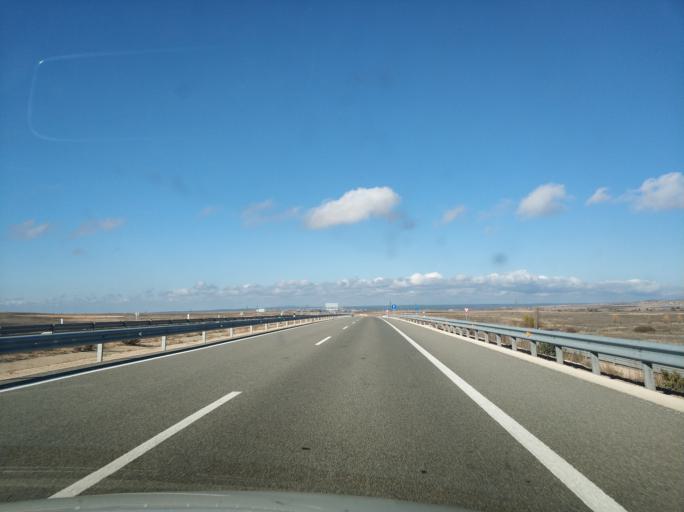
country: ES
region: Castille and Leon
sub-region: Provincia de Soria
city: Coscurita
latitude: 41.4204
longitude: -2.4893
